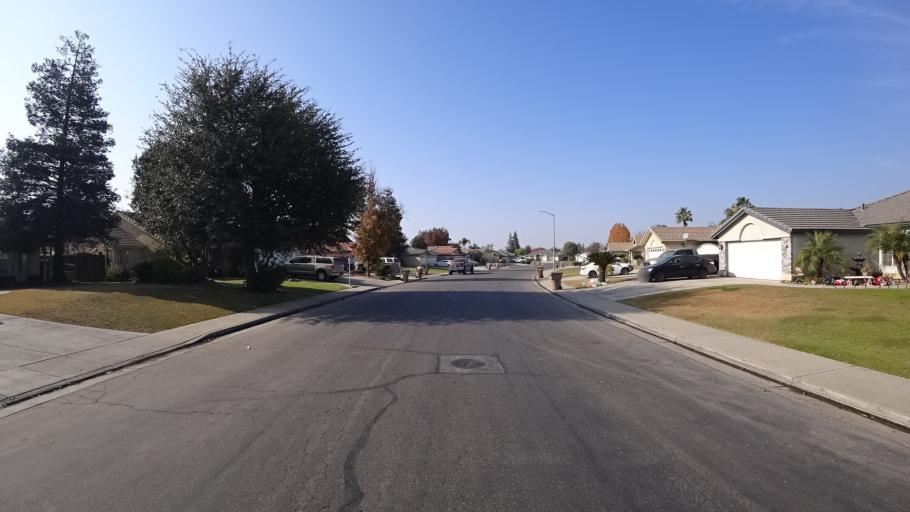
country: US
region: California
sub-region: Kern County
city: Greenacres
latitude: 35.4060
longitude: -119.1120
